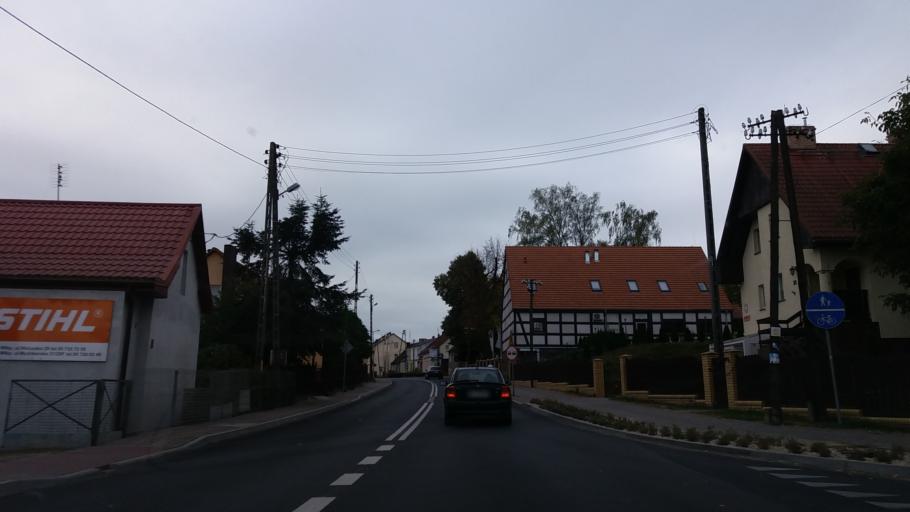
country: PL
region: Lubusz
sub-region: Powiat gorzowski
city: Klodawa
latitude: 52.7894
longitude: 15.2131
